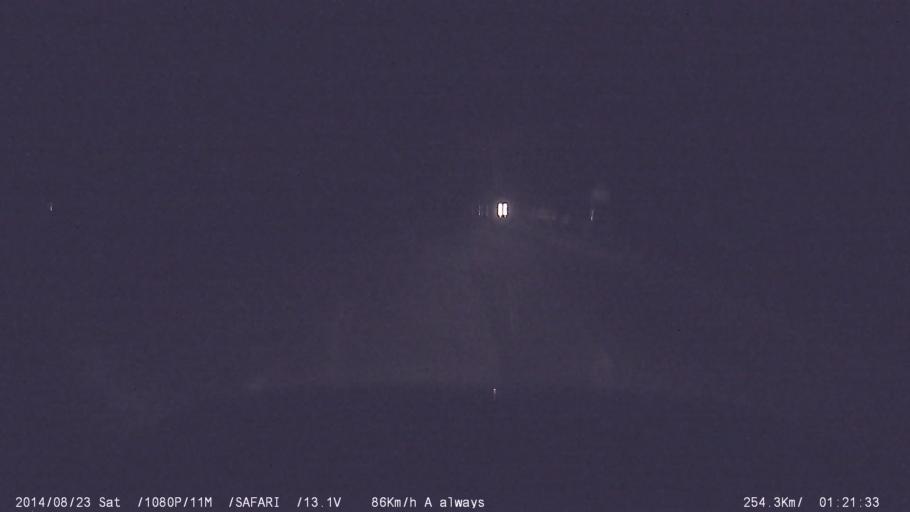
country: IN
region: Tamil Nadu
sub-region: Kancheepuram
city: Kanchipuram
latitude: 12.8767
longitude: 79.6138
